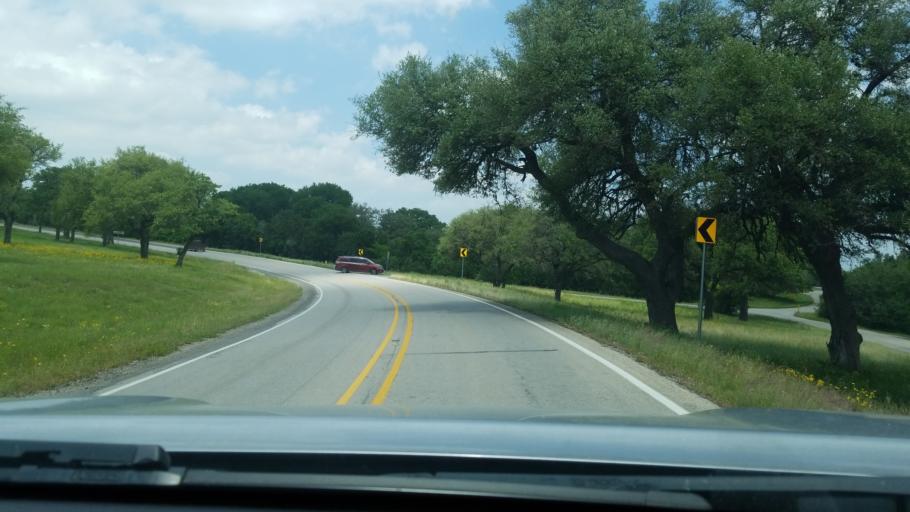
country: US
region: Texas
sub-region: Hays County
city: Dripping Springs
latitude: 30.1482
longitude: -98.0514
